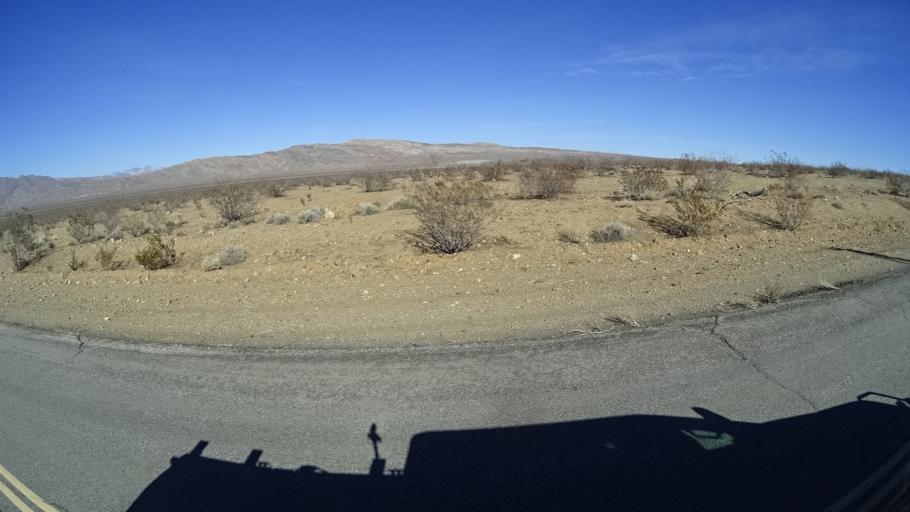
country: US
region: California
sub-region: Kern County
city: Ridgecrest
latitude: 35.3831
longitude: -117.7039
